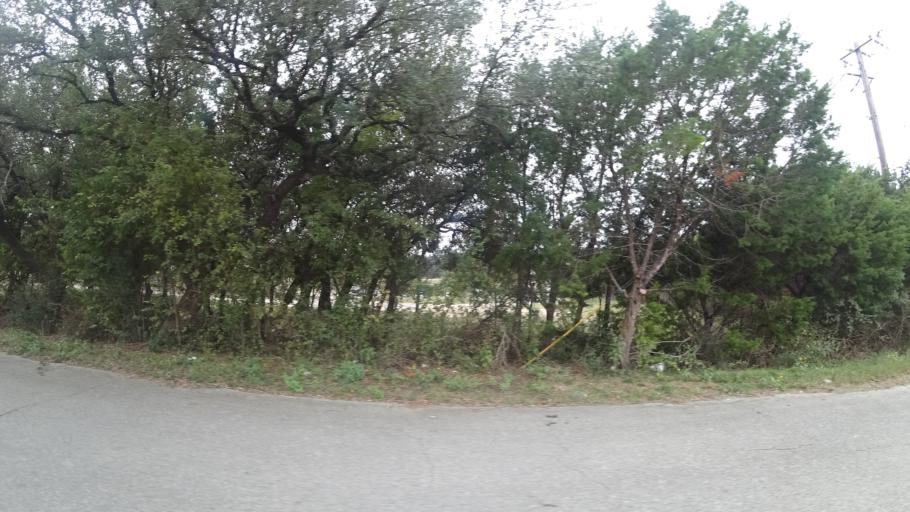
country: US
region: Texas
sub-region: Travis County
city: Lakeway
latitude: 30.3709
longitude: -97.9434
